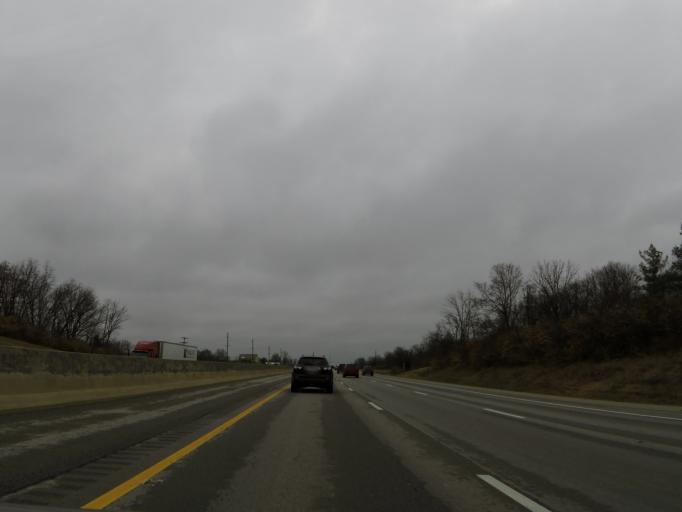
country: US
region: Kentucky
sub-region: Grant County
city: Crittenden
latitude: 38.7624
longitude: -84.6081
